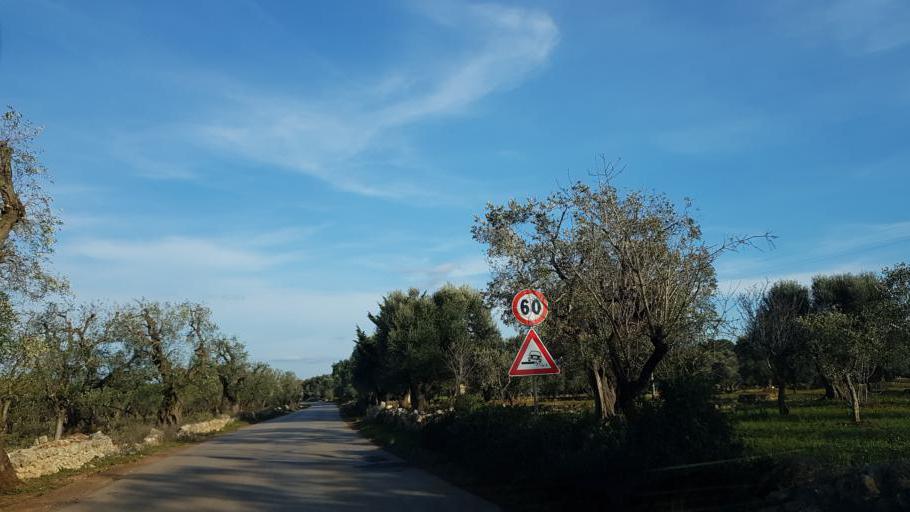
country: IT
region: Apulia
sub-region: Provincia di Brindisi
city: Carovigno
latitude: 40.7059
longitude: 17.6997
